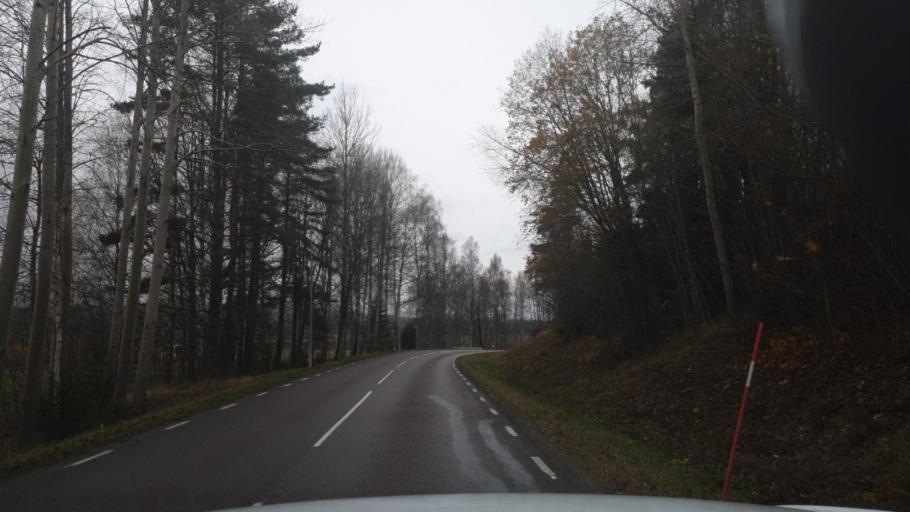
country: SE
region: Vaermland
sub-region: Arvika Kommun
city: Arvika
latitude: 59.5611
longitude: 12.5575
